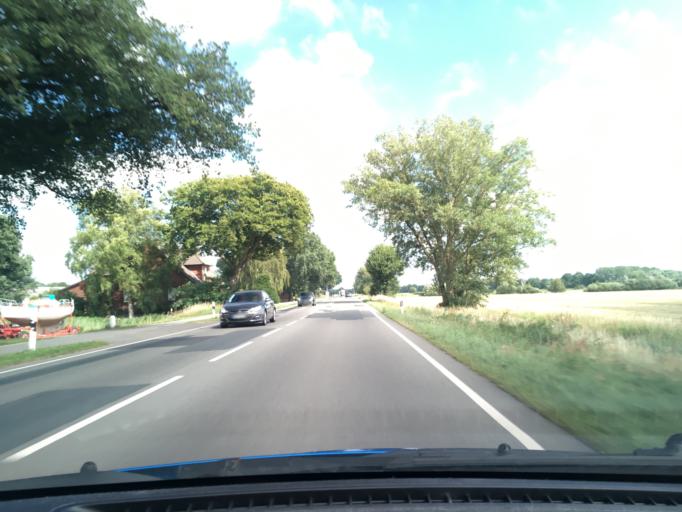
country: DE
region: Lower Saxony
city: Stelle
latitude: 53.3685
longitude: 10.1566
